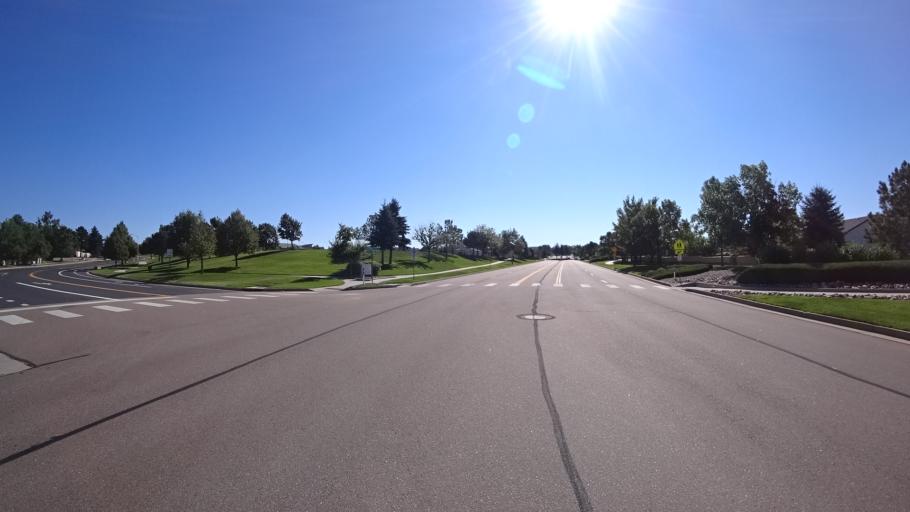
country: US
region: Colorado
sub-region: El Paso County
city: Gleneagle
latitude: 38.9758
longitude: -104.7783
